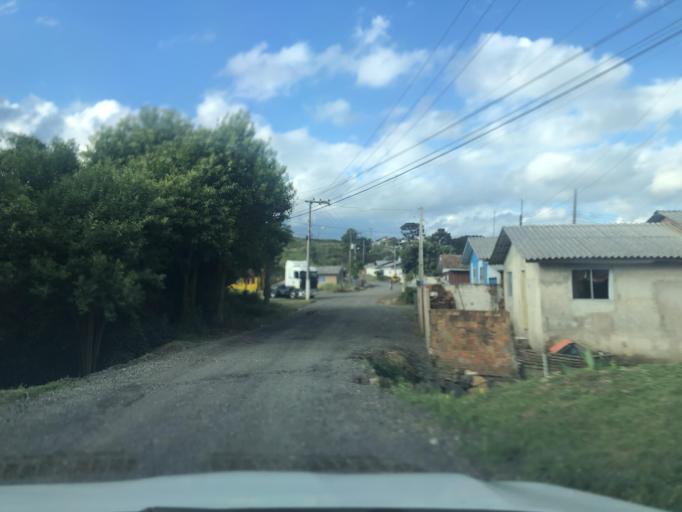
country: BR
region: Santa Catarina
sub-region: Lages
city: Lages
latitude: -27.7951
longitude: -50.3175
